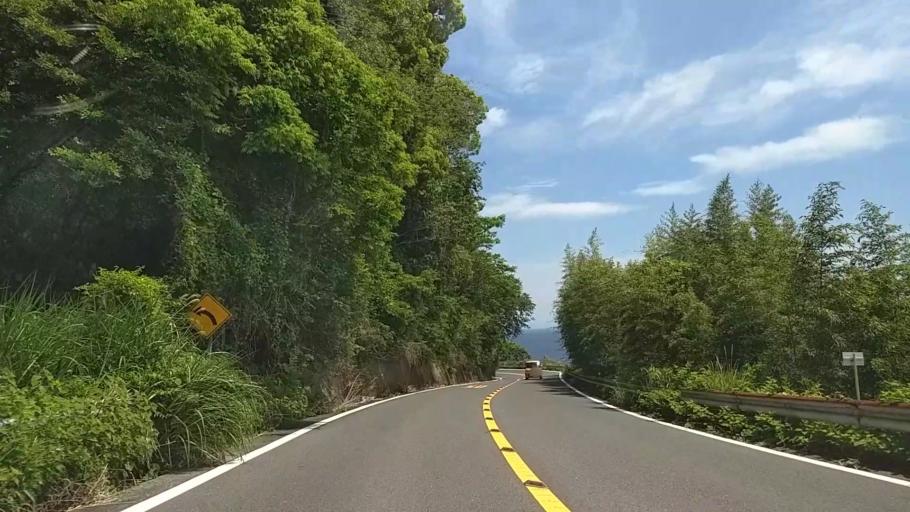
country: JP
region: Kanagawa
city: Yugawara
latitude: 35.1669
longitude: 139.1429
